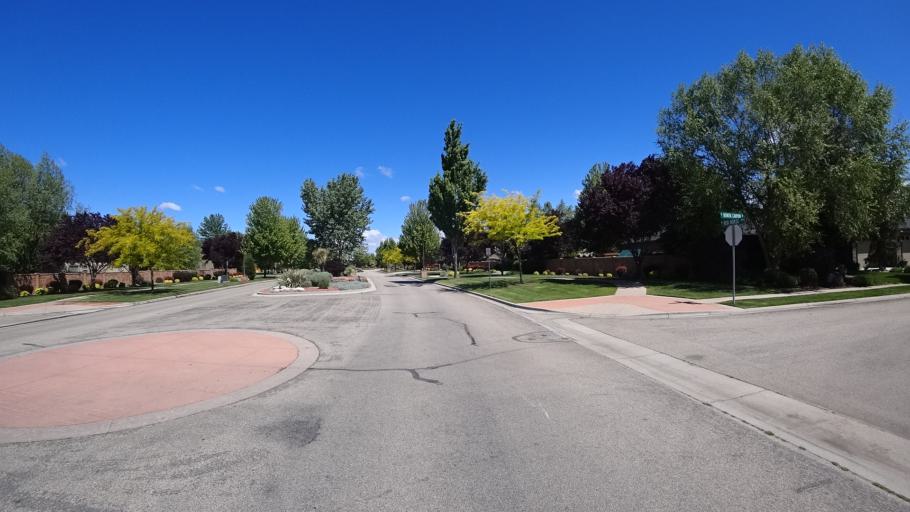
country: US
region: Idaho
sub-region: Ada County
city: Meridian
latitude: 43.6499
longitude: -116.3840
